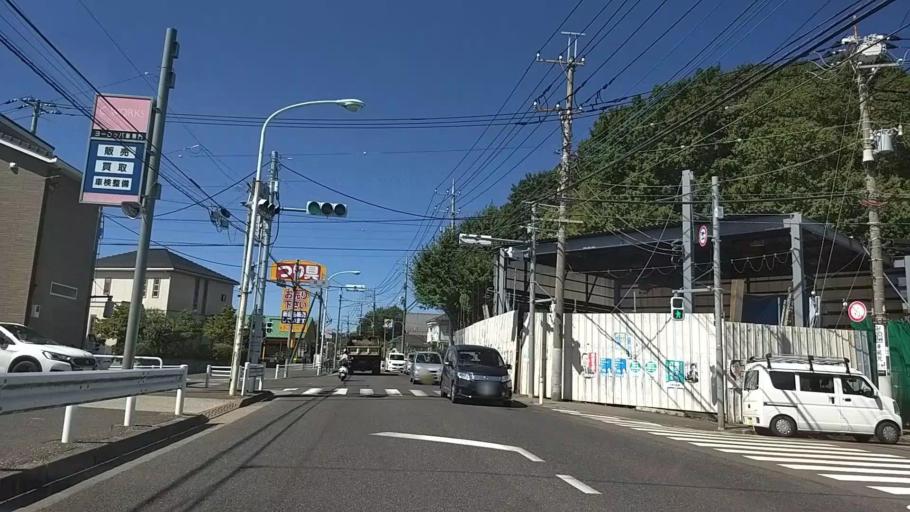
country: JP
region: Tokyo
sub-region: Machida-shi
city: Machida
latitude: 35.5887
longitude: 139.4555
